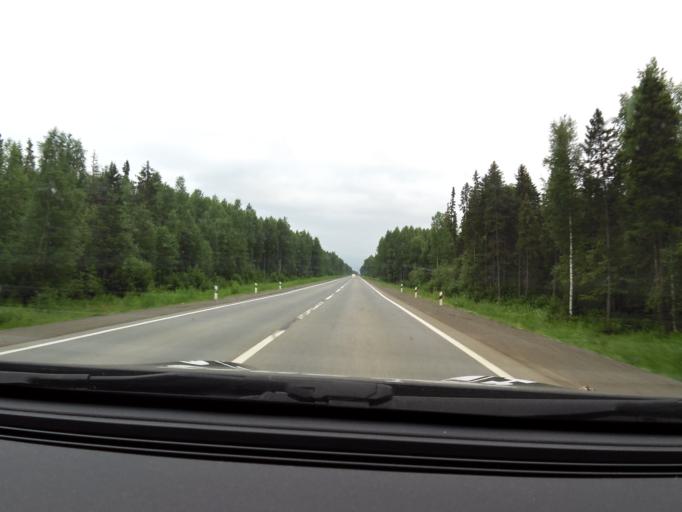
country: RU
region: Perm
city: Zyukayka
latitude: 58.3329
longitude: 54.7243
